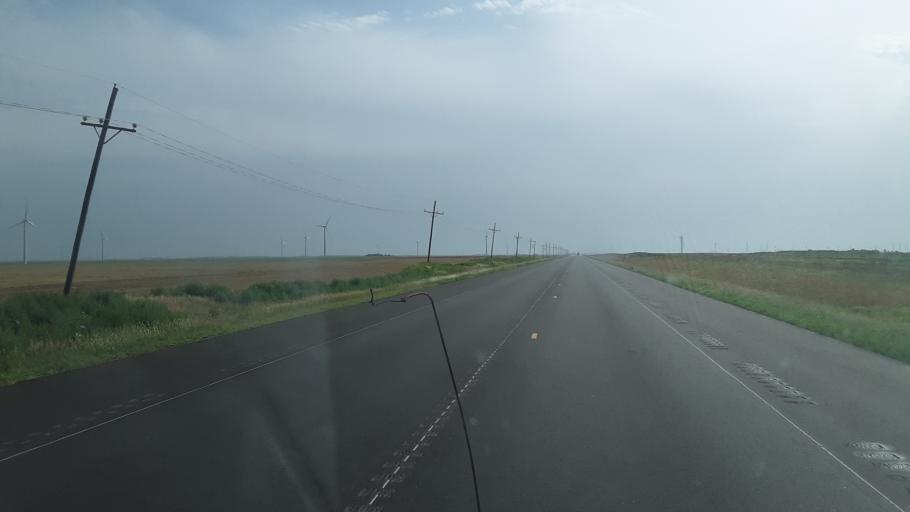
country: US
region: Kansas
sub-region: Ford County
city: Dodge City
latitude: 37.7956
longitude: -99.8669
